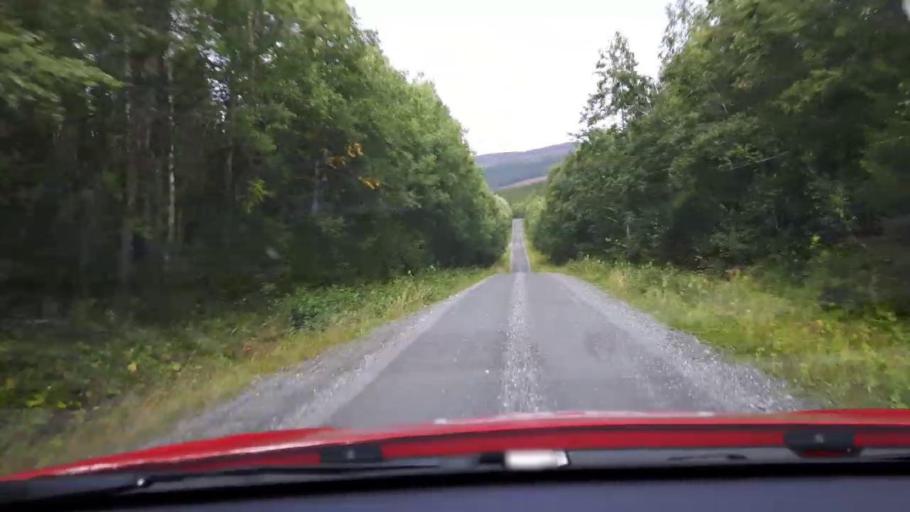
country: SE
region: Jaemtland
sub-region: Are Kommun
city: Are
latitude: 63.7995
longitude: 13.1104
